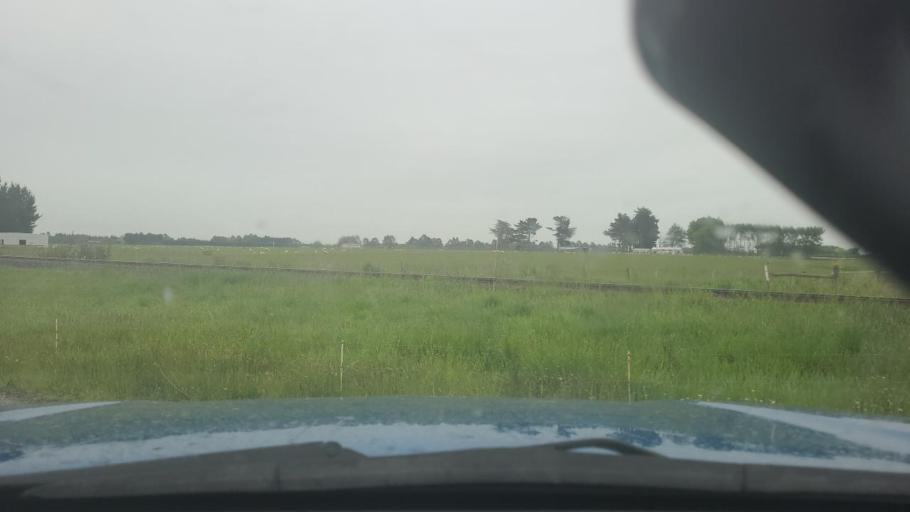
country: NZ
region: Southland
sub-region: Invercargill City
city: Invercargill
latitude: -46.3810
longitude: 168.4954
